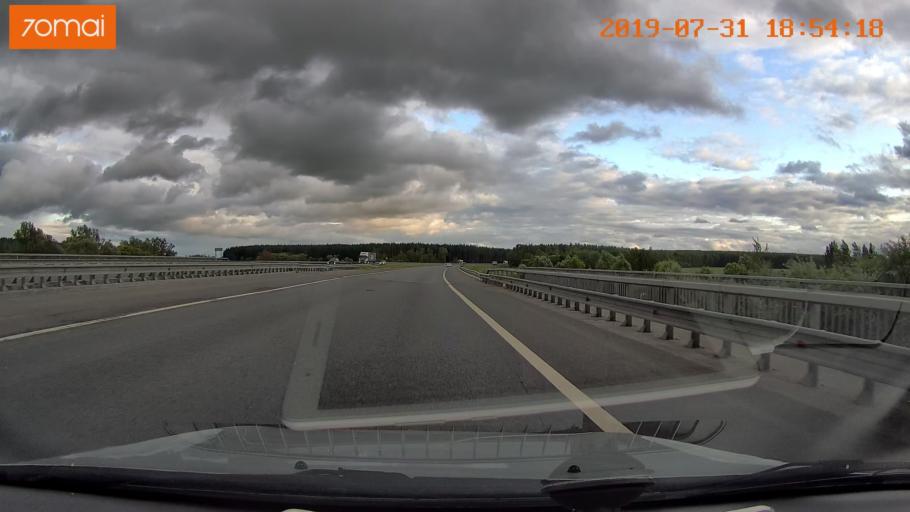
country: RU
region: Moskovskaya
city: Raduzhnyy
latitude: 55.1923
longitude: 38.6674
